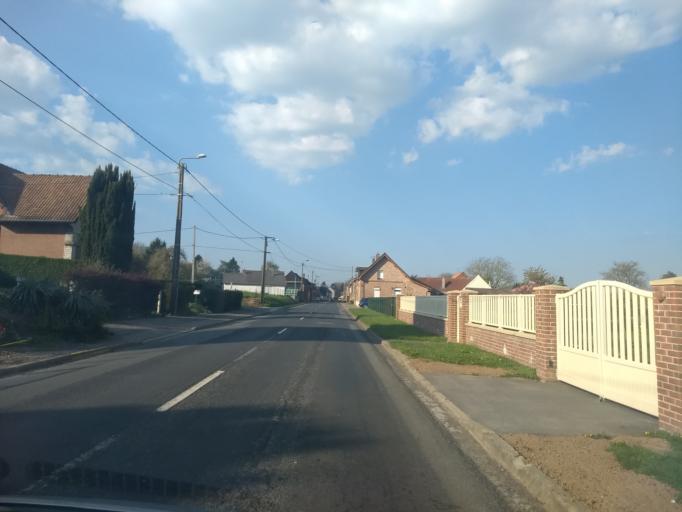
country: FR
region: Picardie
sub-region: Departement de la Somme
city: Albert
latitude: 50.0824
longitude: 2.6069
